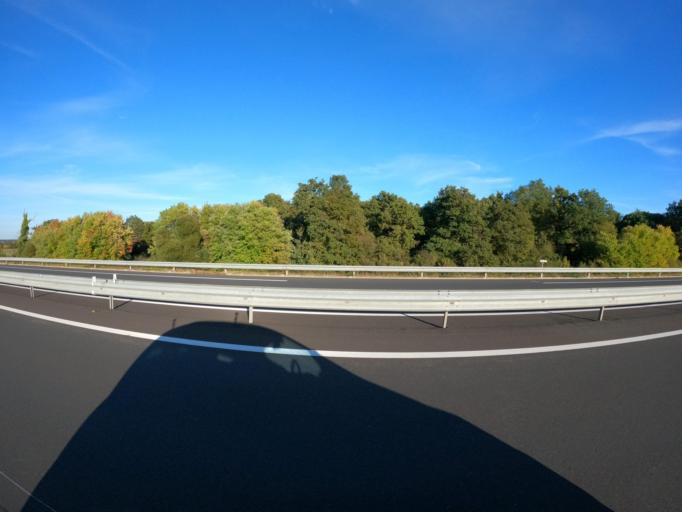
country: FR
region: Pays de la Loire
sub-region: Departement de la Vendee
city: Mortagne-sur-Sevre
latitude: 46.9810
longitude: -0.9179
